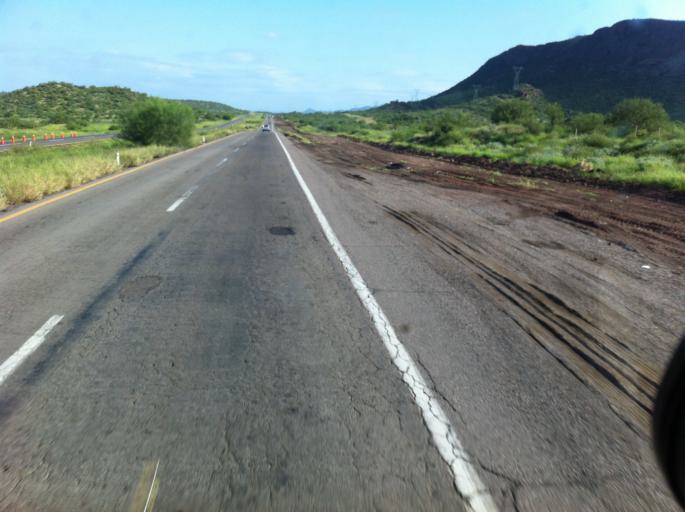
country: MX
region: Sonora
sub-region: Empalme
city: La Palma
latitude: 28.4689
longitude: -111.0477
